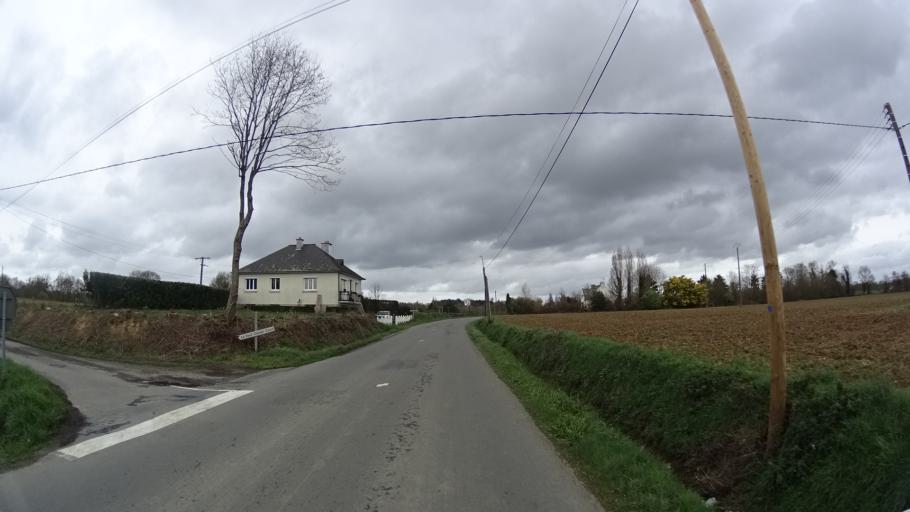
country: FR
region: Brittany
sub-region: Departement d'Ille-et-Vilaine
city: Saint-Gilles
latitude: 48.1661
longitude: -1.8301
